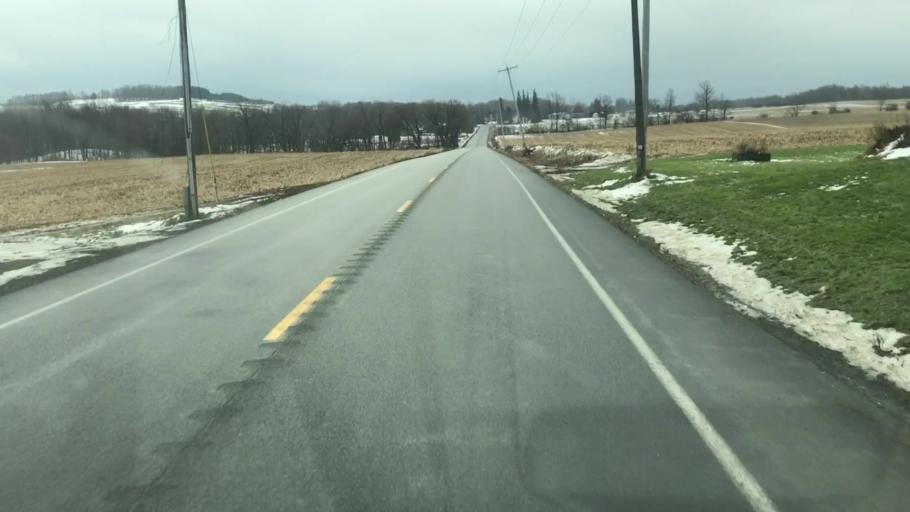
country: US
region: New York
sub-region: Cayuga County
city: Moravia
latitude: 42.8161
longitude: -76.3489
